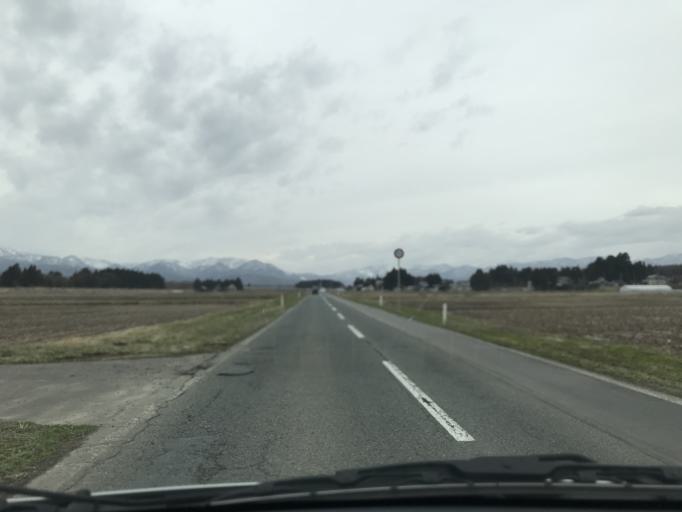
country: JP
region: Iwate
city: Kitakami
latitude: 39.2921
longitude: 141.0434
